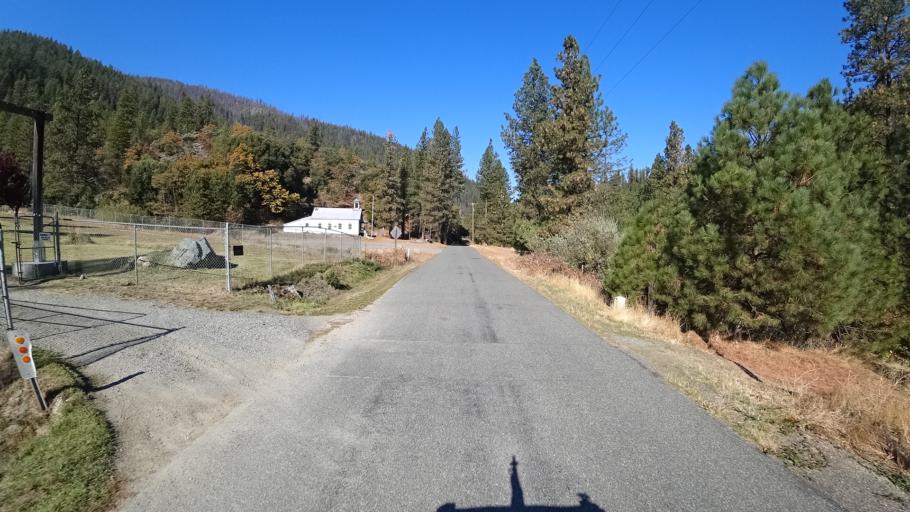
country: US
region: California
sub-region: Siskiyou County
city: Yreka
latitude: 41.7439
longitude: -123.0050
